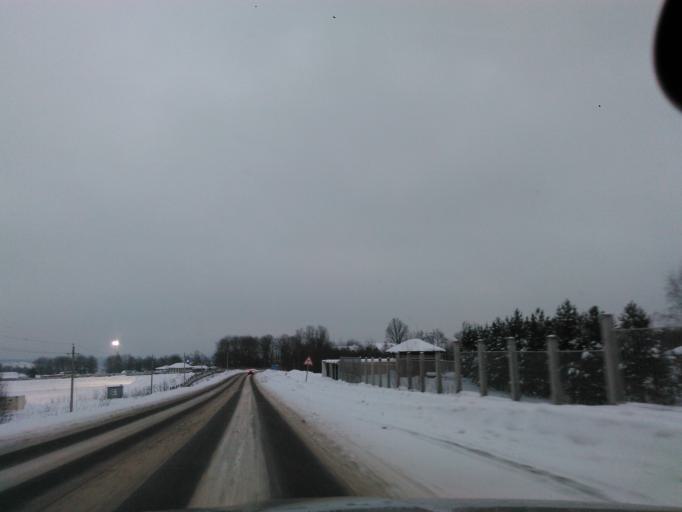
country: RU
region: Moskovskaya
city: Yakhroma
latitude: 56.2688
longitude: 37.4639
